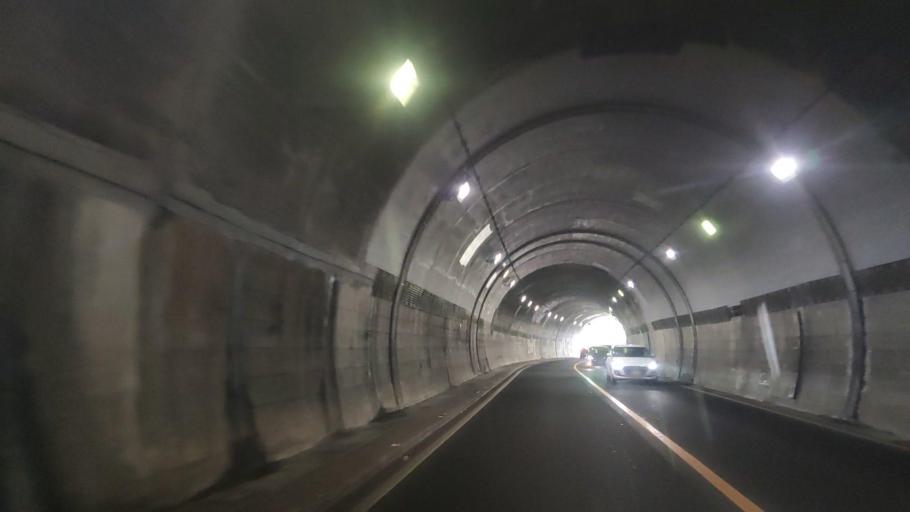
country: JP
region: Tottori
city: Tottori
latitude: 35.5316
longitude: 134.2296
